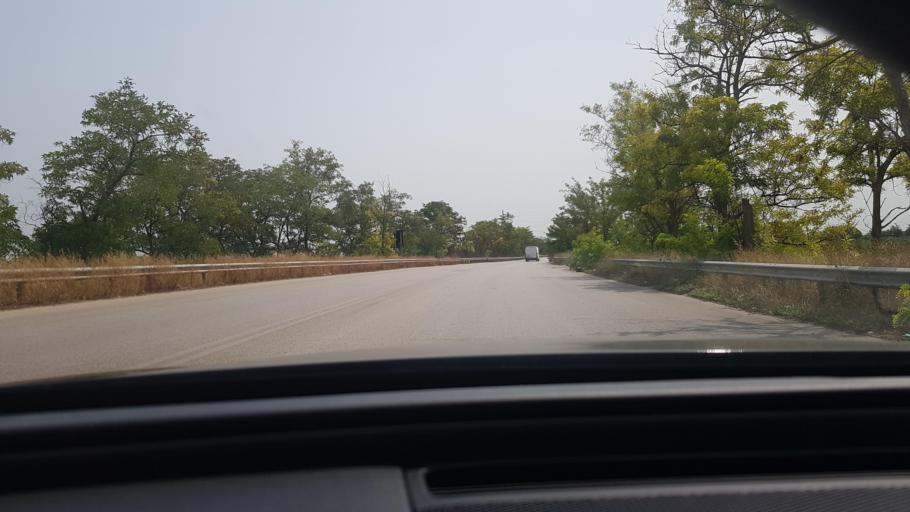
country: IT
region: Apulia
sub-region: Provincia di Barletta - Andria - Trani
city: Andria
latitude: 41.2146
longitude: 16.2680
